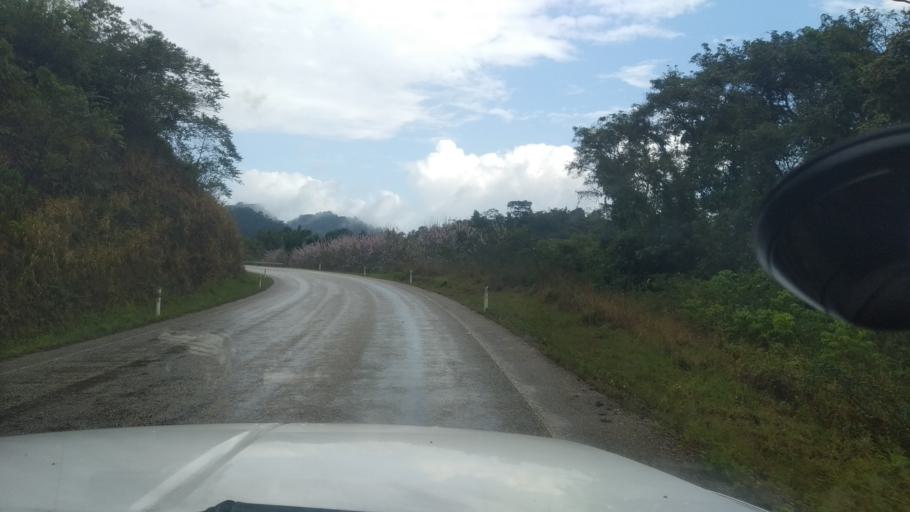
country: GT
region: Peten
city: San Luis
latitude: 16.1885
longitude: -89.1831
